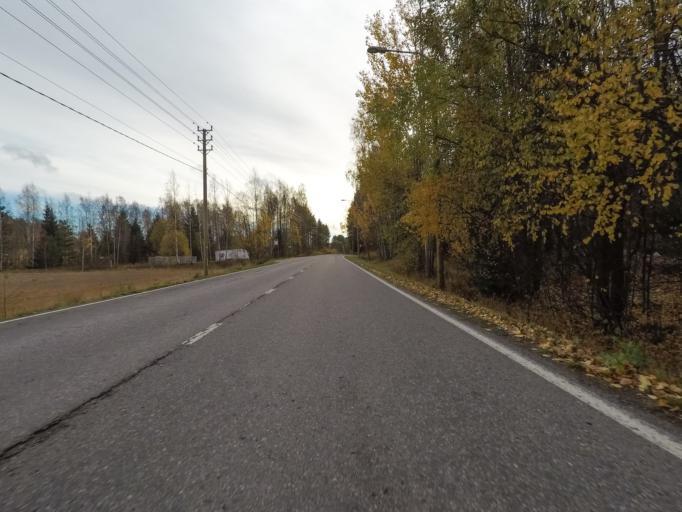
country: FI
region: Uusimaa
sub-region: Helsinki
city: Vantaa
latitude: 60.2652
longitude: 25.1399
